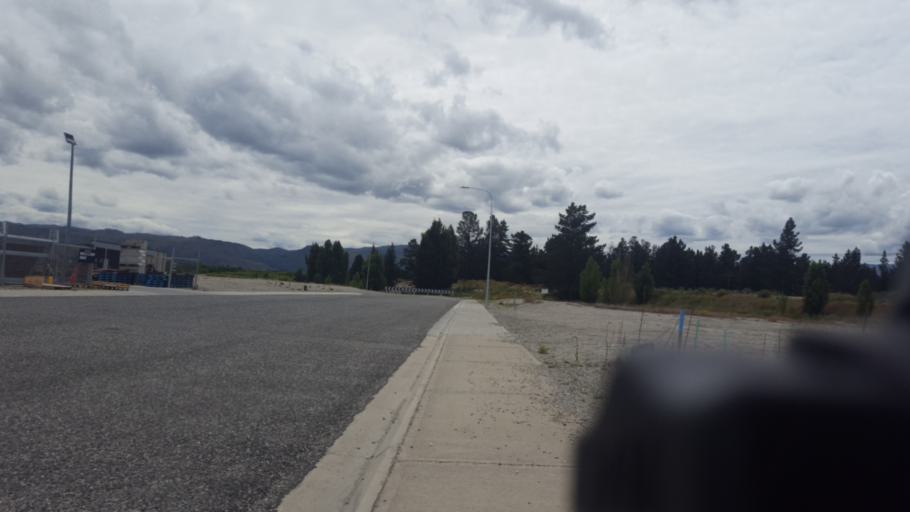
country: NZ
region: Otago
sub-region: Queenstown-Lakes District
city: Wanaka
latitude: -45.2467
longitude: 169.3720
